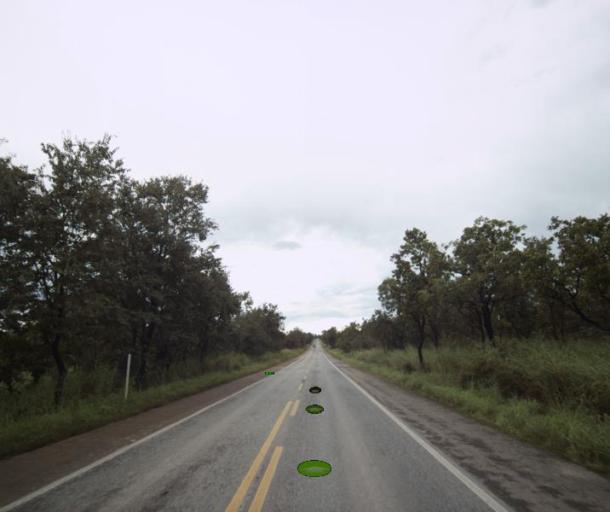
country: BR
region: Goias
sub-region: Porangatu
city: Porangatu
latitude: -13.6709
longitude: -49.0283
